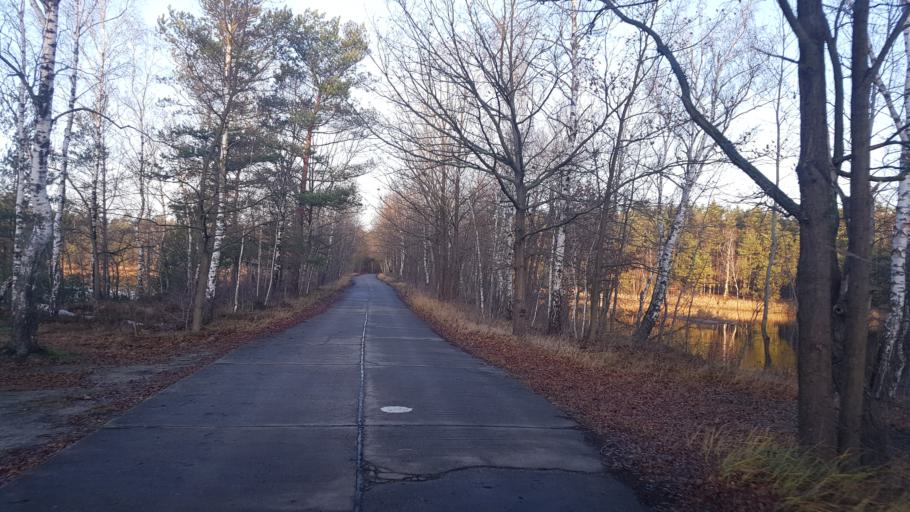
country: DE
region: Brandenburg
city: Ruckersdorf
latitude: 51.5905
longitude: 13.5873
